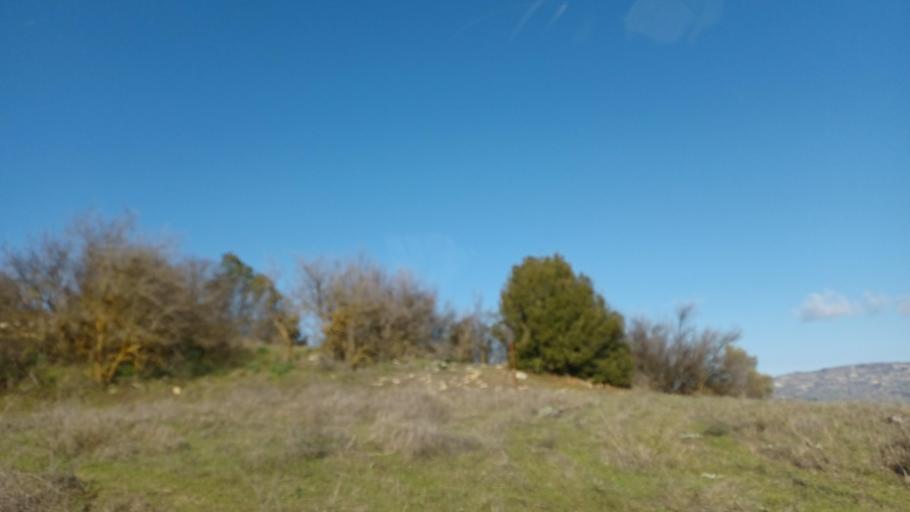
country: CY
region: Limassol
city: Pachna
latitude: 34.8147
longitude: 32.6709
